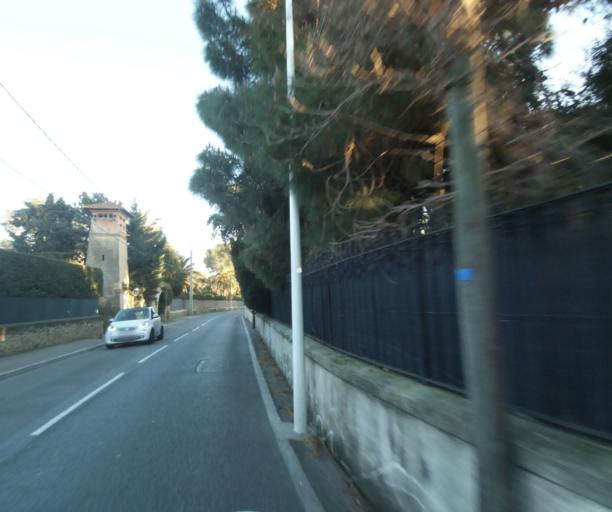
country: FR
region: Provence-Alpes-Cote d'Azur
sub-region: Departement des Alpes-Maritimes
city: Antibes
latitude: 43.5622
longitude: 7.1276
